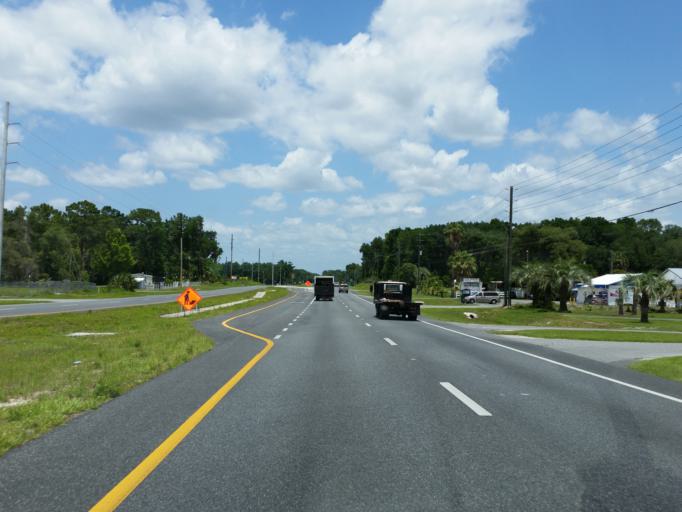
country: US
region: Florida
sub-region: Marion County
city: Belleview
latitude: 28.9764
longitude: -82.0411
